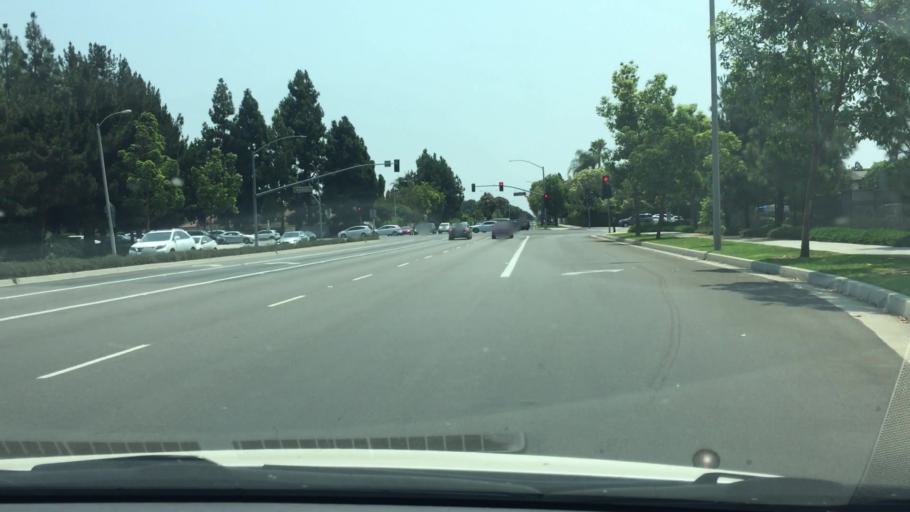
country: US
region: California
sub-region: Orange County
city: North Tustin
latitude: 33.7166
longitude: -117.7775
